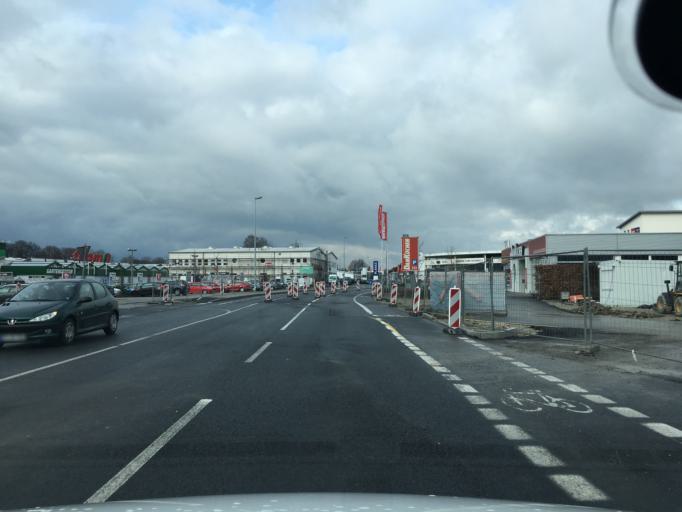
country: DE
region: Bavaria
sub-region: Upper Bavaria
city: Kolbermoor
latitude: 47.8488
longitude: 12.0810
